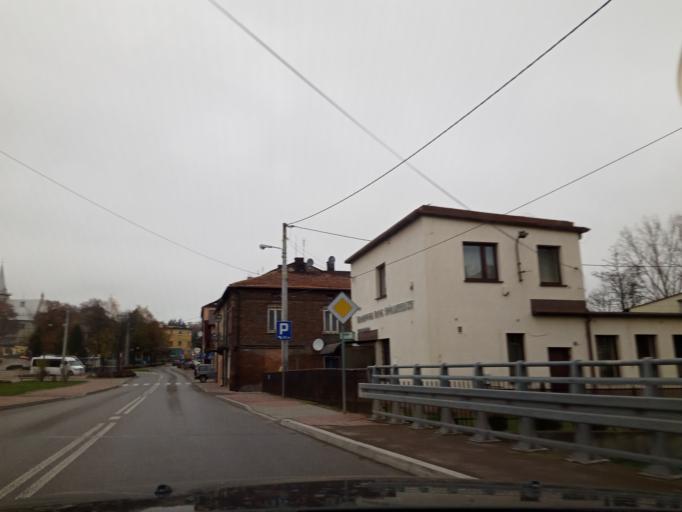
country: PL
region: Swietokrzyskie
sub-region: Powiat pinczowski
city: Dzialoszyce
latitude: 50.3643
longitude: 20.3532
